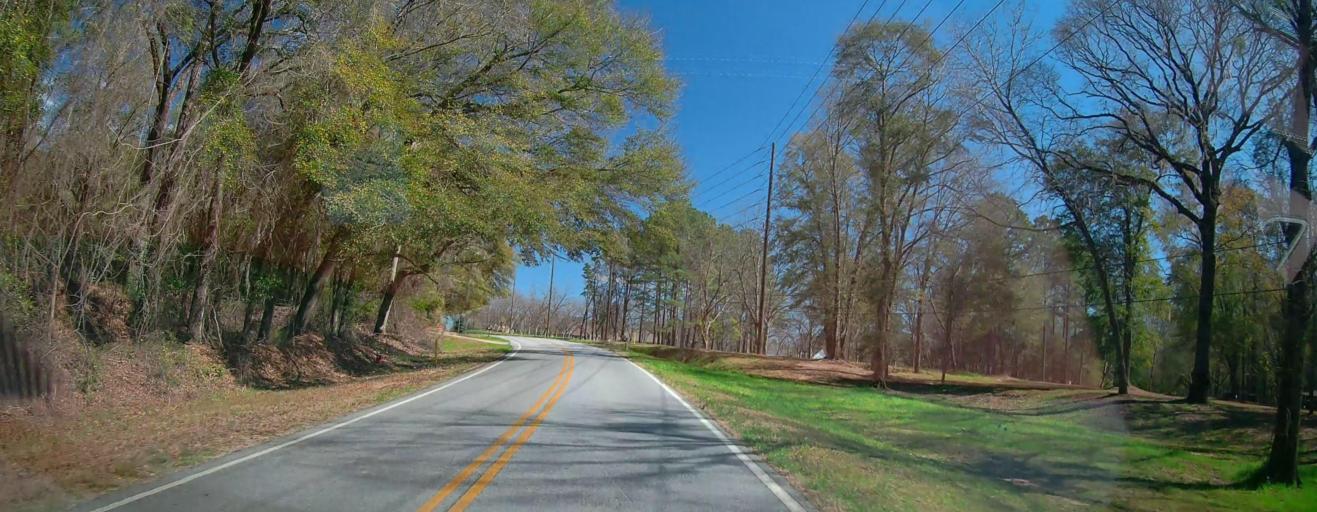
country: US
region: Georgia
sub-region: Houston County
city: Perry
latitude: 32.4900
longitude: -83.6515
